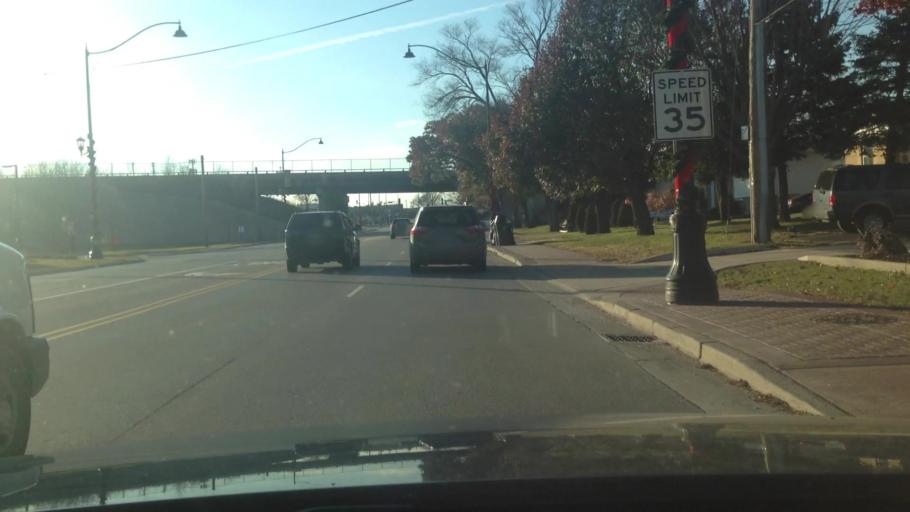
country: US
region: Illinois
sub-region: DuPage County
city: Bensenville
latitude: 41.9610
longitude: -87.9575
